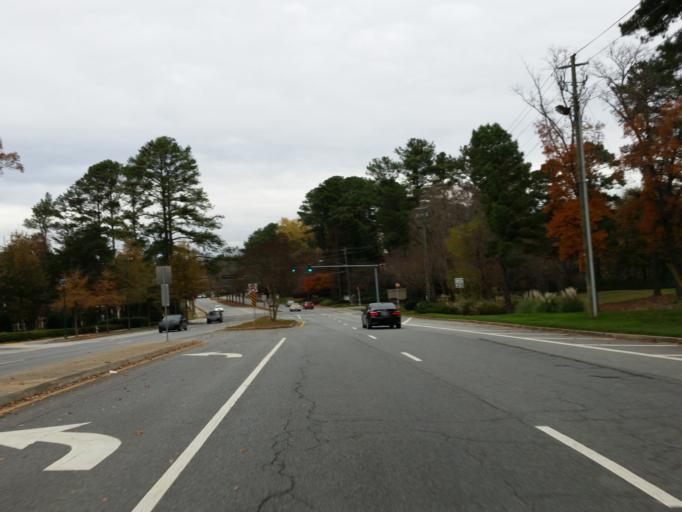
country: US
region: Georgia
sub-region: Fulton County
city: Sandy Springs
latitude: 33.9113
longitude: -84.3618
